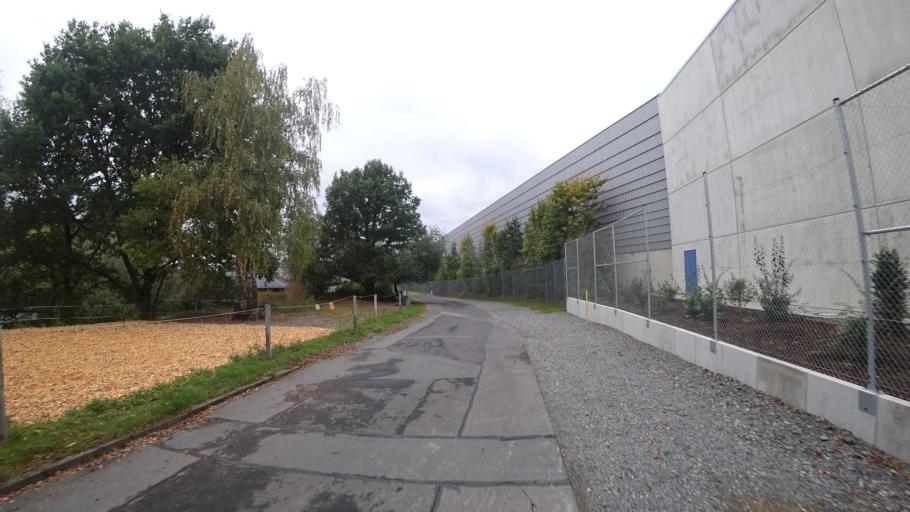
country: DE
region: Rheinland-Pfalz
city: Selters
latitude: 50.5360
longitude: 7.7530
